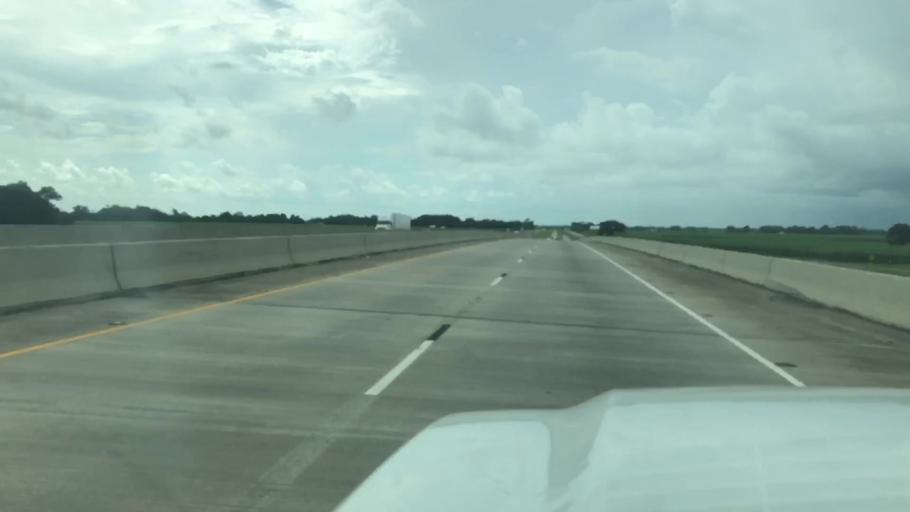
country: US
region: Louisiana
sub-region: Iberia Parish
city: Jeanerette
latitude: 29.9197
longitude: -91.7284
